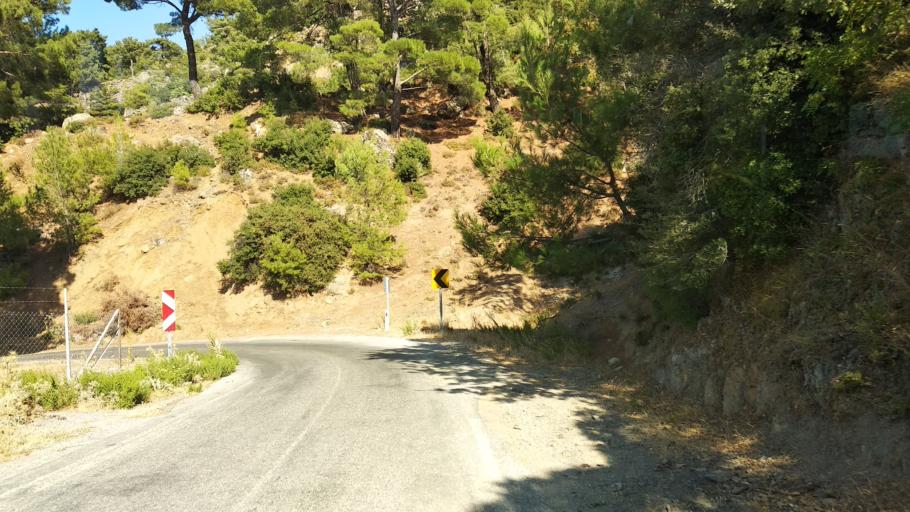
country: TR
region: Izmir
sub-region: Seferihisar
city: Seferhisar
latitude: 38.3160
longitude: 26.9570
